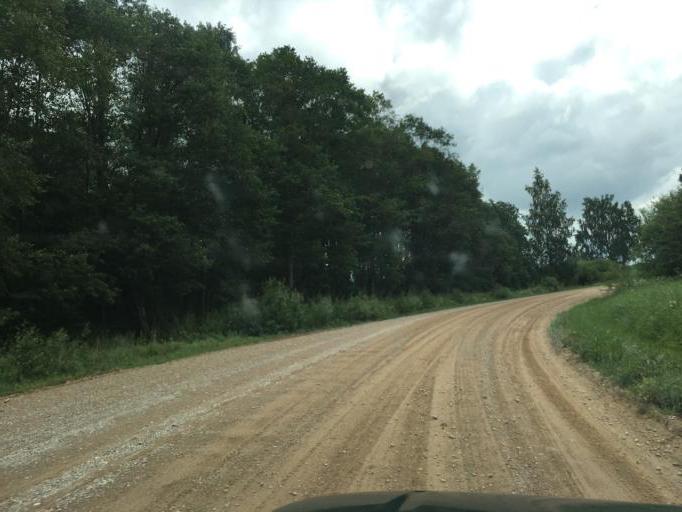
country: LV
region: Balvu Rajons
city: Balvi
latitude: 57.3463
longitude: 27.4210
